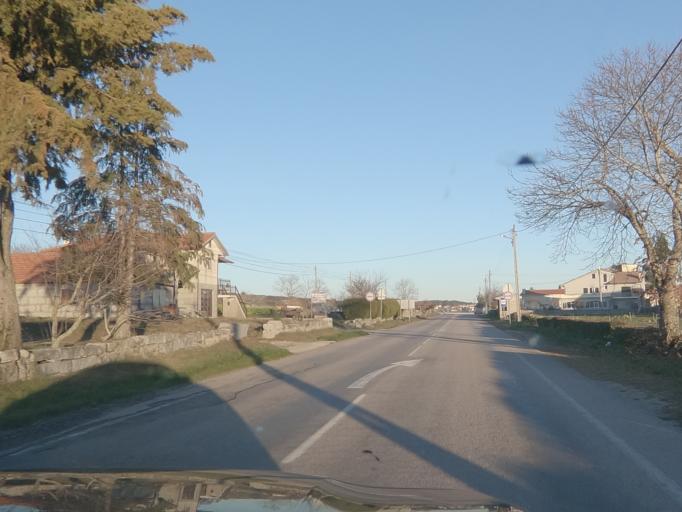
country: PT
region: Vila Real
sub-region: Vila Pouca de Aguiar
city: Vila Pouca de Aguiar
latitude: 41.4999
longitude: -7.7079
